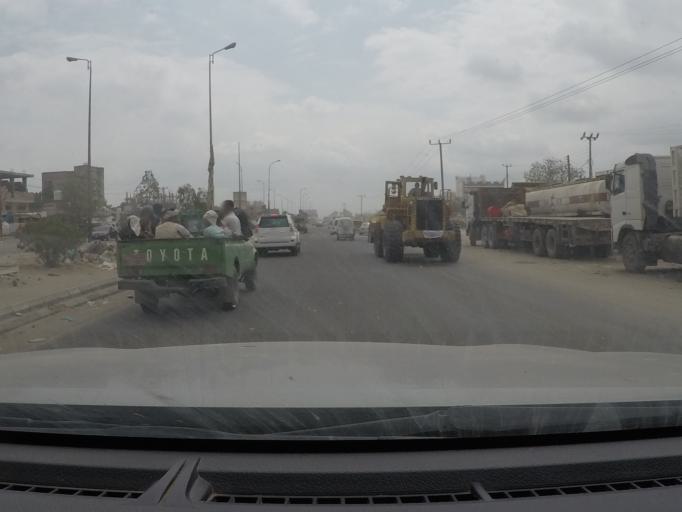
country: YE
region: Lahij
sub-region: Al  Hawtah
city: Lahij
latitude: 12.9982
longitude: 44.9266
